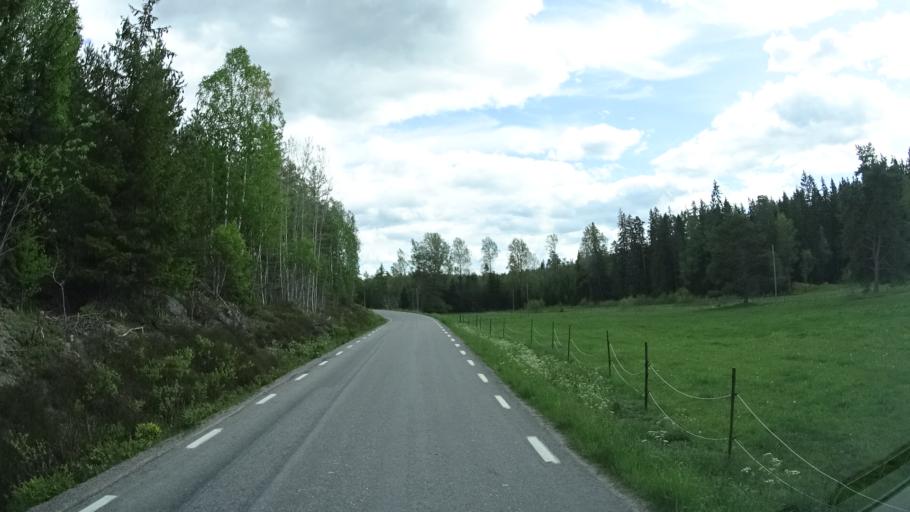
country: SE
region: OEstergoetland
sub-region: Finspangs Kommun
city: Finspang
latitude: 58.6057
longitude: 15.7487
